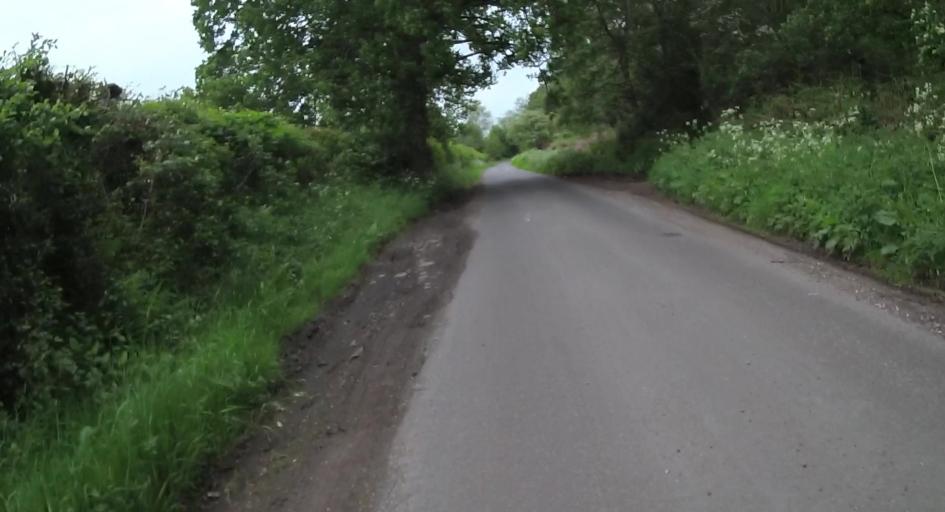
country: GB
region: England
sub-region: West Berkshire
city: Stratfield Mortimer
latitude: 51.3542
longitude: -1.0653
